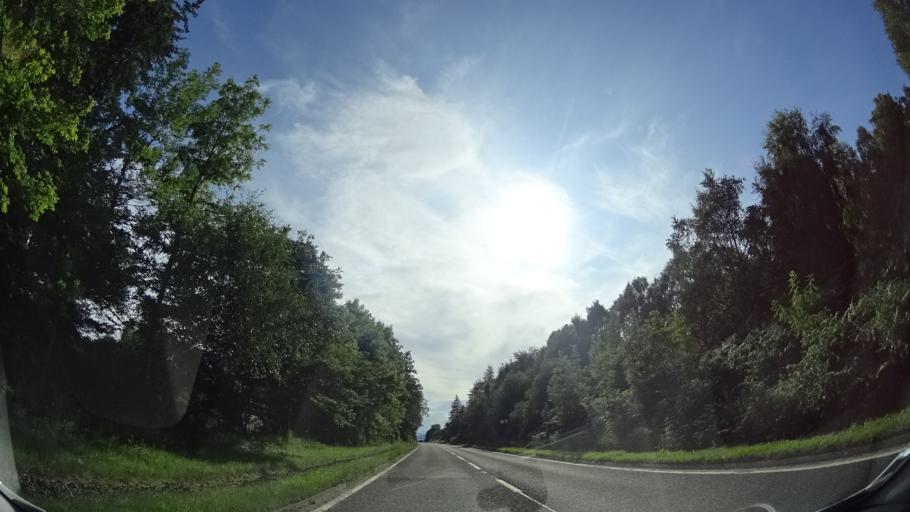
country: GB
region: Scotland
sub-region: Highland
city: Conon Bridge
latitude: 57.5647
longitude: -4.4811
